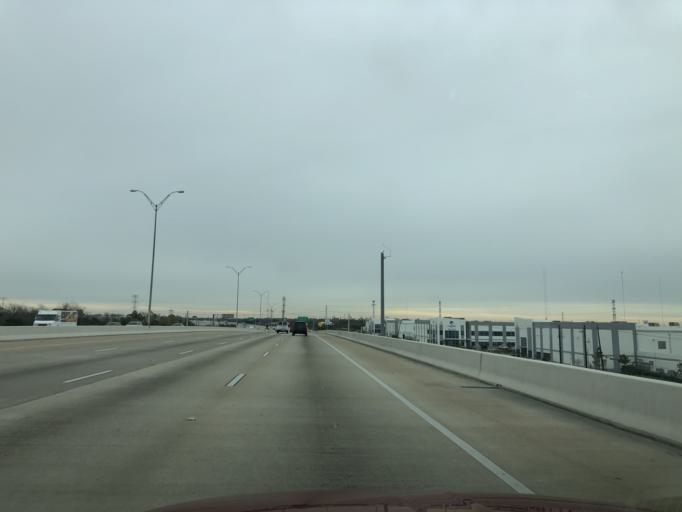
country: US
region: Texas
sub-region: Fort Bend County
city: Missouri City
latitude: 29.6262
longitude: -95.5179
